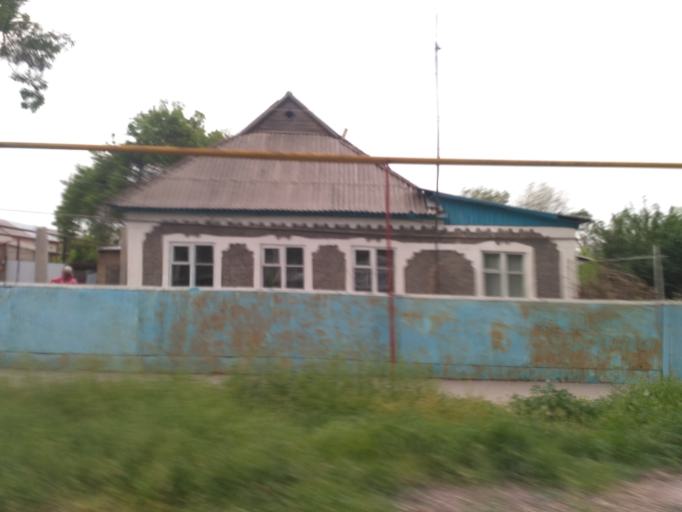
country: KZ
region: Almaty Oblysy
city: Burunday
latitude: 43.4542
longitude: 76.7228
